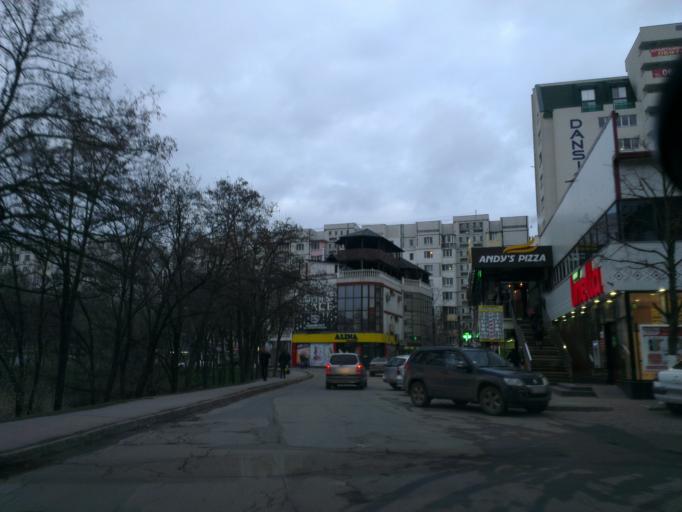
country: MD
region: Chisinau
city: Chisinau
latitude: 47.0370
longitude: 28.8276
